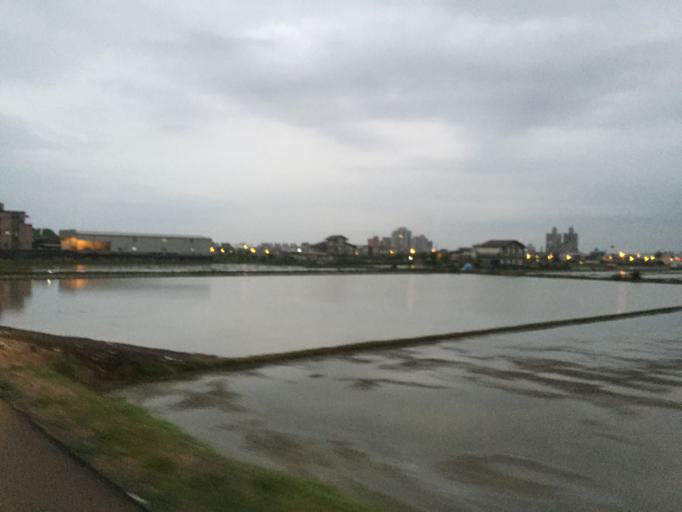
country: TW
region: Taiwan
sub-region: Yilan
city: Yilan
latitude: 24.7695
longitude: 121.7425
